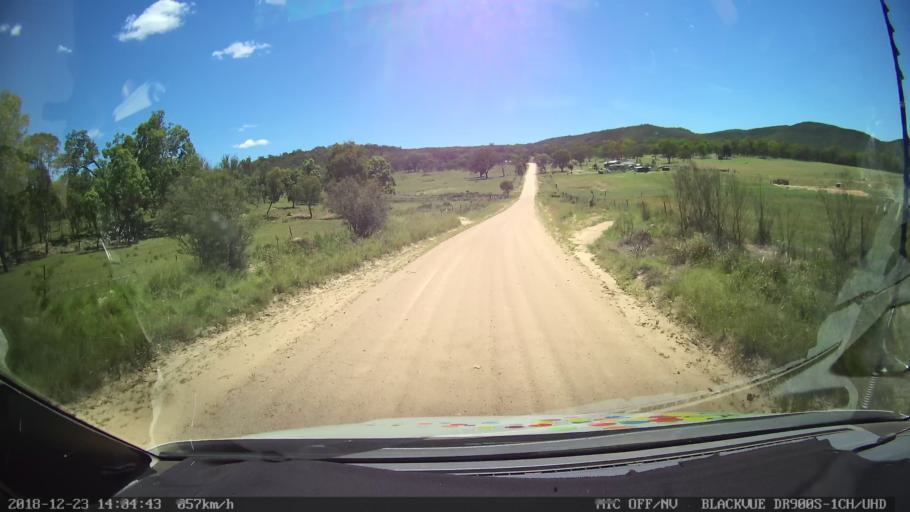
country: AU
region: New South Wales
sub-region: Tamworth Municipality
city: Manilla
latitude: -30.6232
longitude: 151.0878
